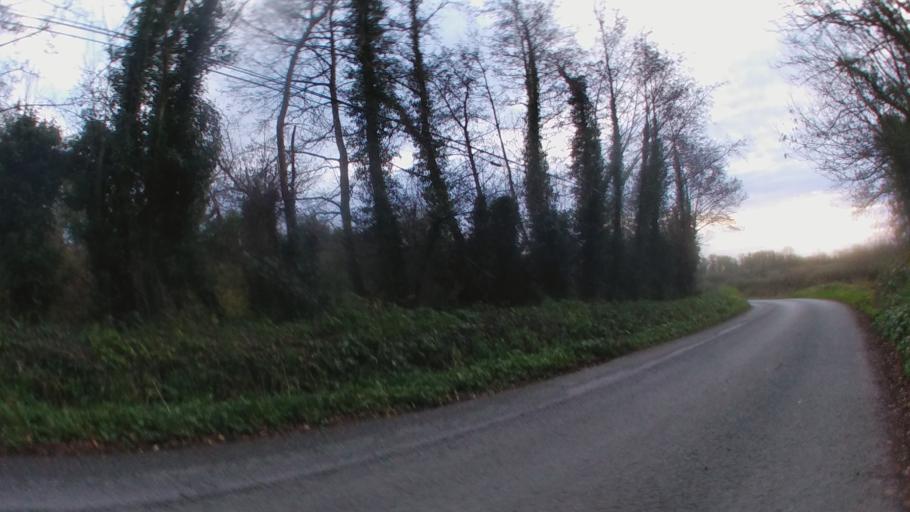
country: IE
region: Leinster
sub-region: Kilkenny
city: Kilkenny
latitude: 52.6935
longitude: -7.1715
